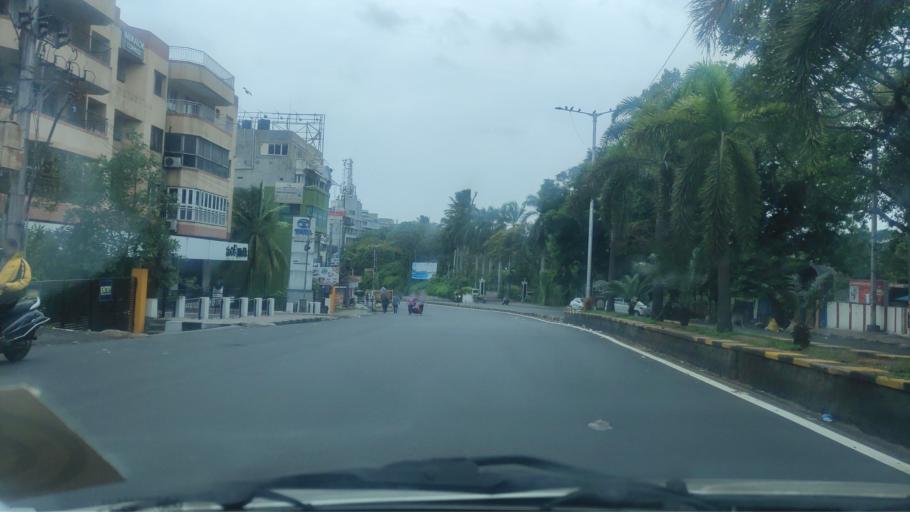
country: IN
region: Telangana
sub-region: Hyderabad
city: Hyderabad
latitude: 17.4120
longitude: 78.4497
